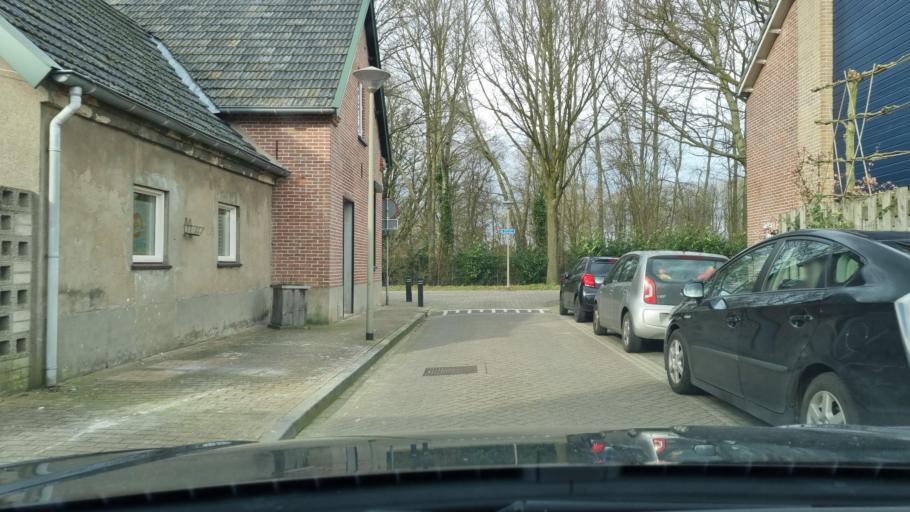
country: NL
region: Gelderland
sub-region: Gemeente Zevenaar
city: Zevenaar
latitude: 51.8624
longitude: 6.0555
